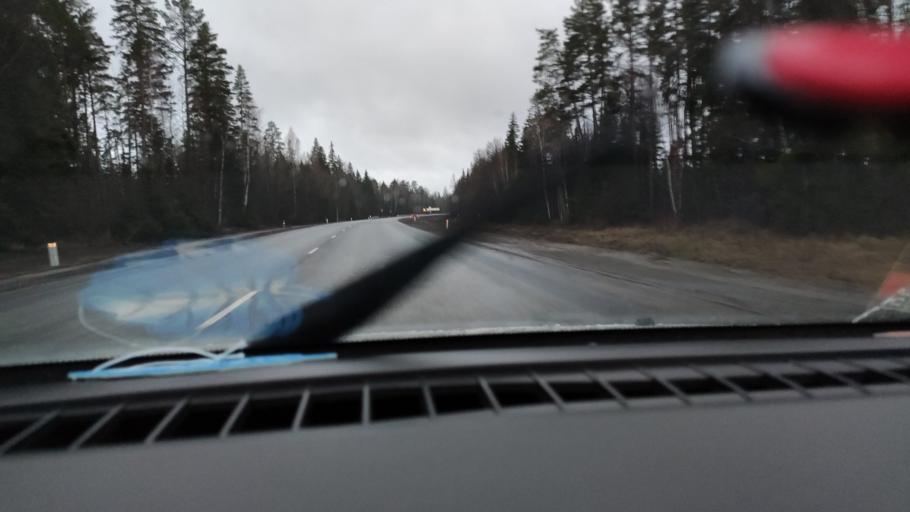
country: RU
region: Udmurtiya
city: Alnashi
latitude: 56.0915
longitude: 52.4457
